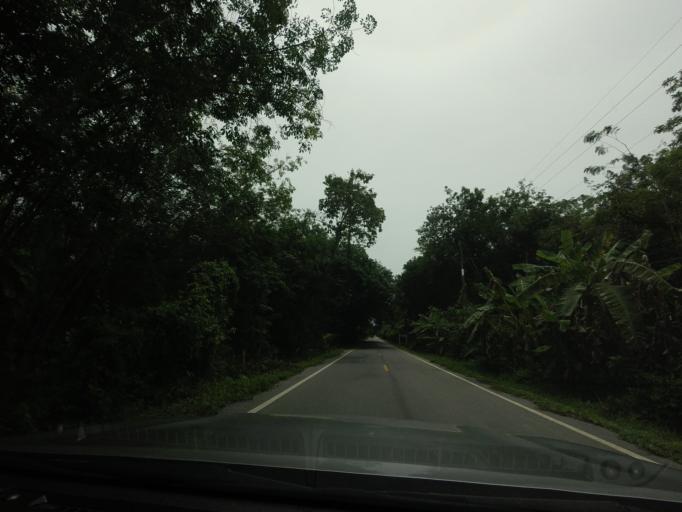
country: TH
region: Pattani
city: Kapho
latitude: 6.6000
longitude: 101.5314
